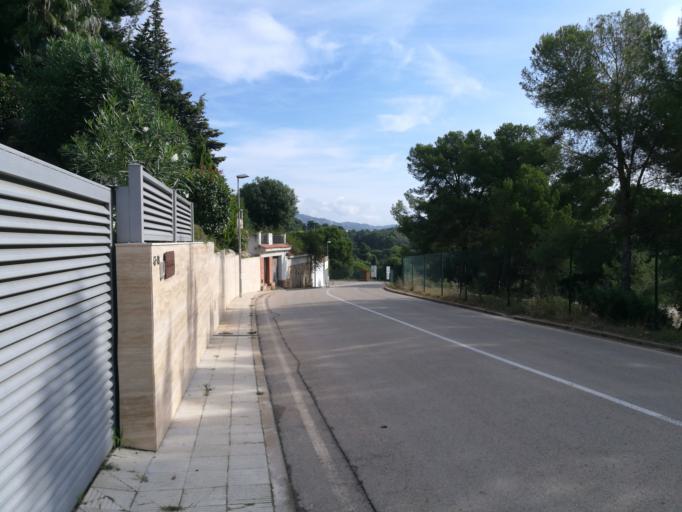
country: ES
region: Catalonia
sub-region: Provincia de Girona
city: Blanes
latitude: 41.6875
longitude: 2.8121
